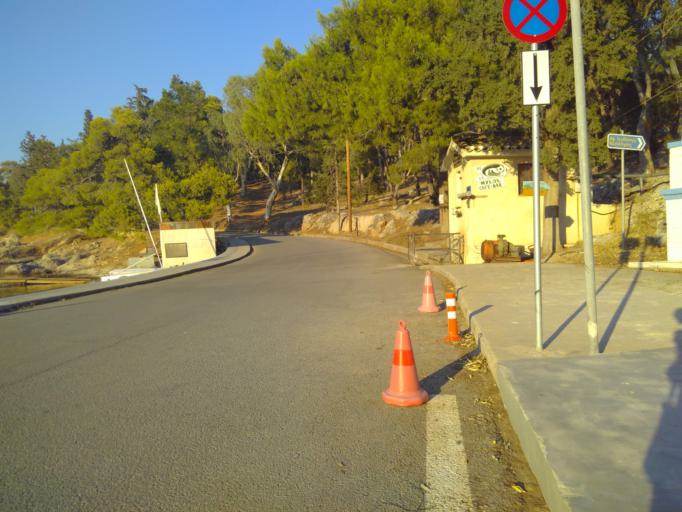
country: GR
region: Central Greece
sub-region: Nomos Fokidos
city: Itea
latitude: 38.3756
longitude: 22.3887
